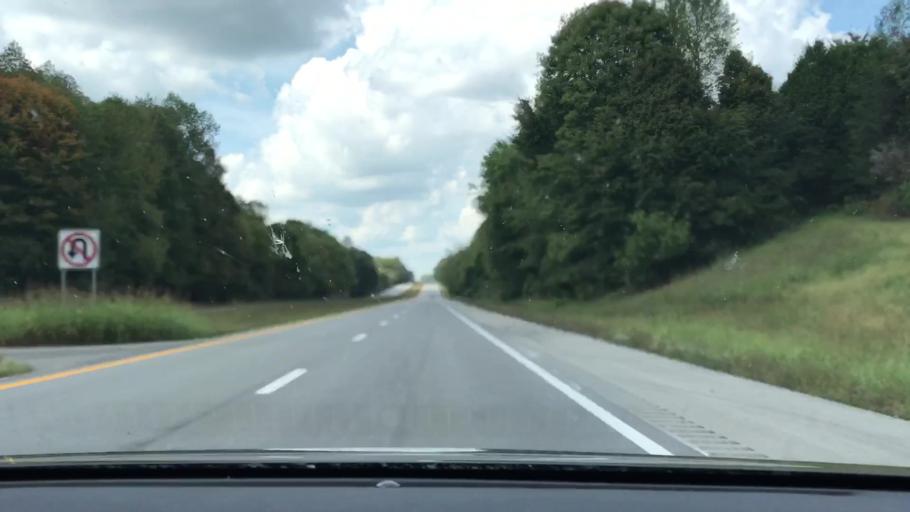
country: US
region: Kentucky
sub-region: Adair County
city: Columbia
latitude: 37.0801
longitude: -85.2429
